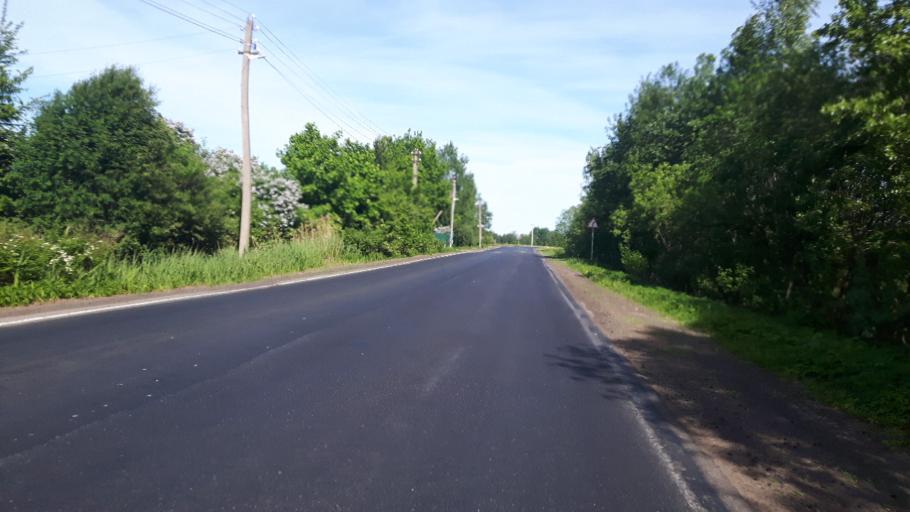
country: RU
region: Leningrad
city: Ivangorod
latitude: 59.4187
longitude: 28.3555
